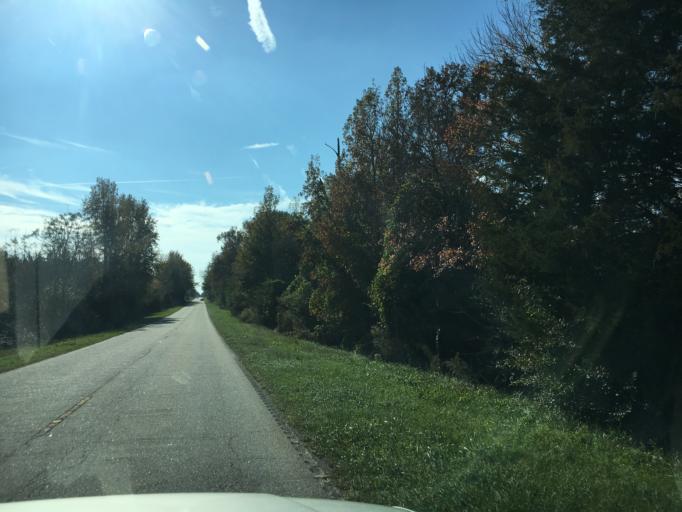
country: US
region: South Carolina
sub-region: Anderson County
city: Iva
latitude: 34.3659
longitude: -82.7150
